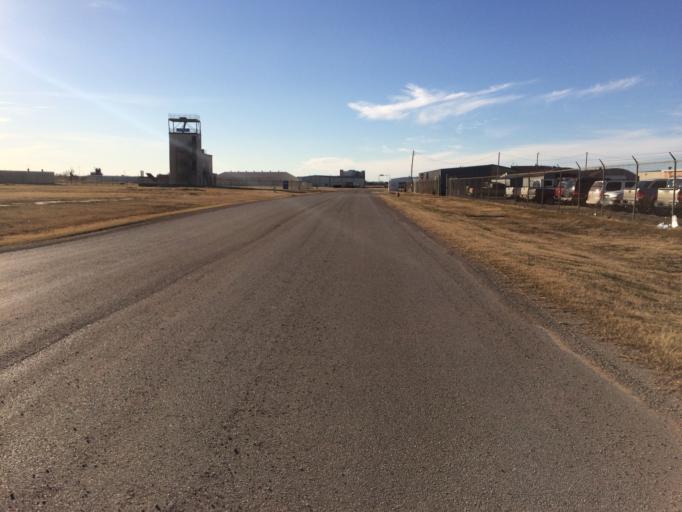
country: US
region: Oklahoma
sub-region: Cleveland County
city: Norman
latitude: 35.2439
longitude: -97.4603
